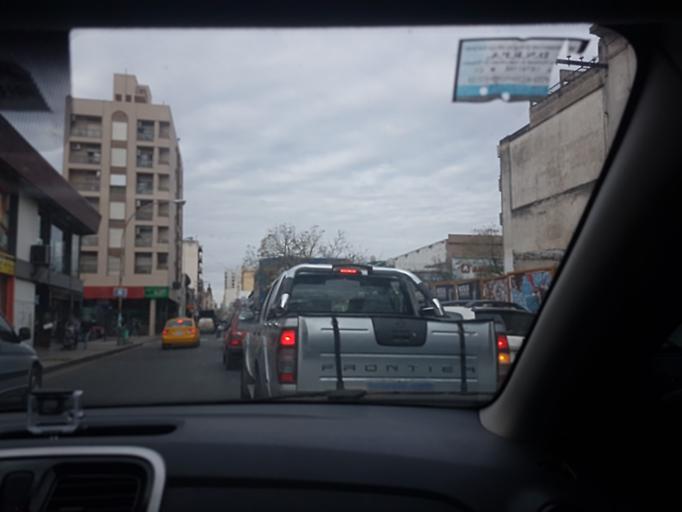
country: AR
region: Cordoba
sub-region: Departamento de Capital
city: Cordoba
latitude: -31.4105
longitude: -64.1787
